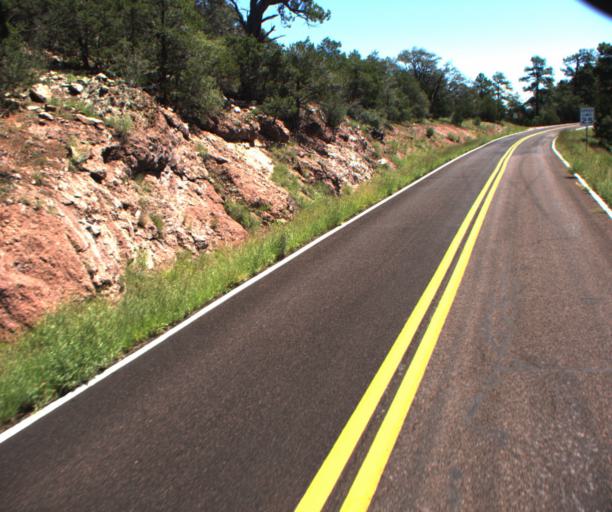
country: US
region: Arizona
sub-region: Greenlee County
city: Morenci
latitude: 33.4112
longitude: -109.3583
